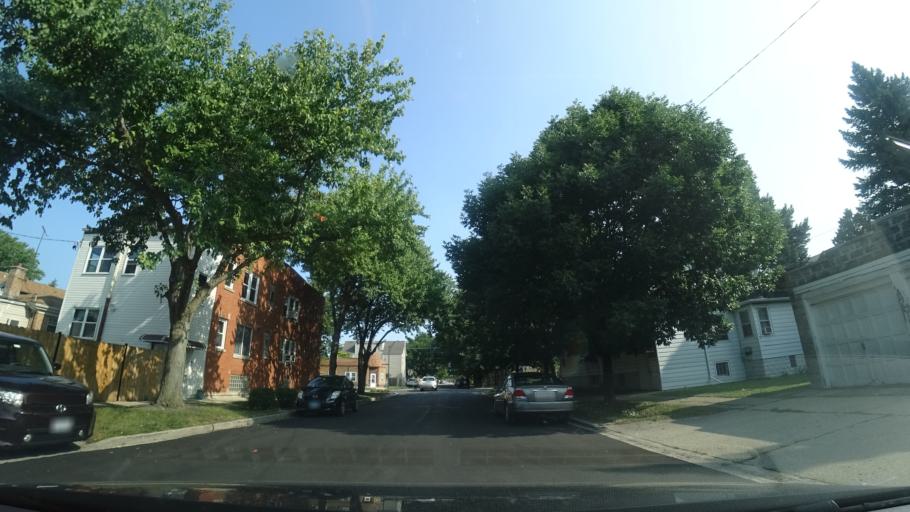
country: US
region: Illinois
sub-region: Cook County
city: Lincolnwood
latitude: 41.9739
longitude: -87.7552
